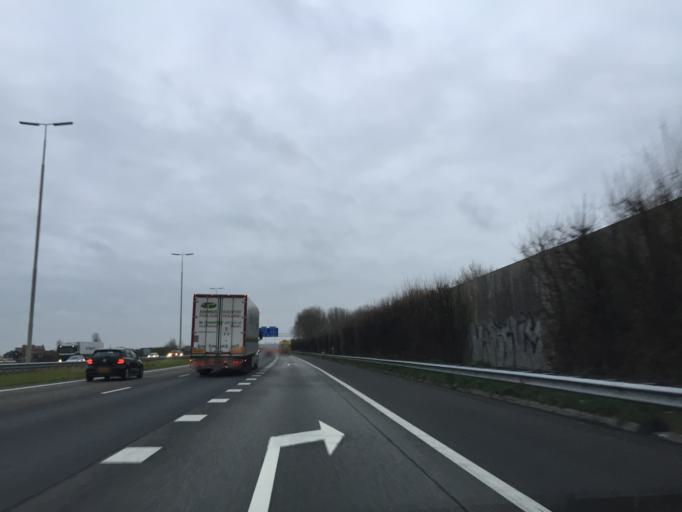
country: NL
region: South Holland
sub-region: Gemeente Leidschendam-Voorburg
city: Voorburg
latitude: 52.0821
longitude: 4.4100
